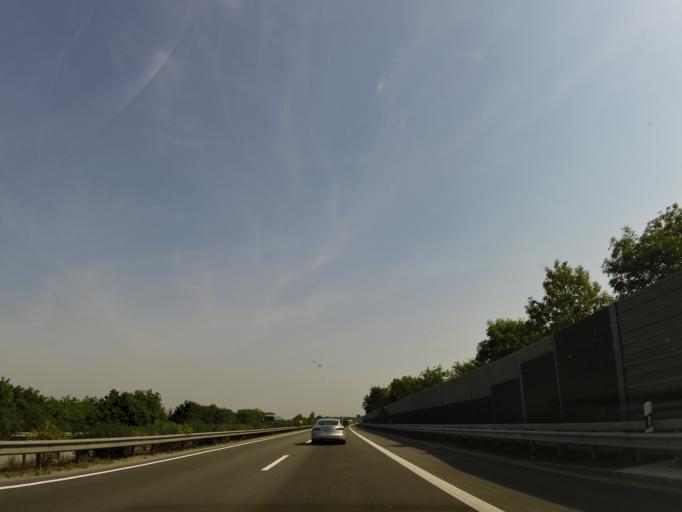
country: DE
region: Rheinland-Pfalz
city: Grossniedesheim
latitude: 49.6054
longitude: 8.2886
